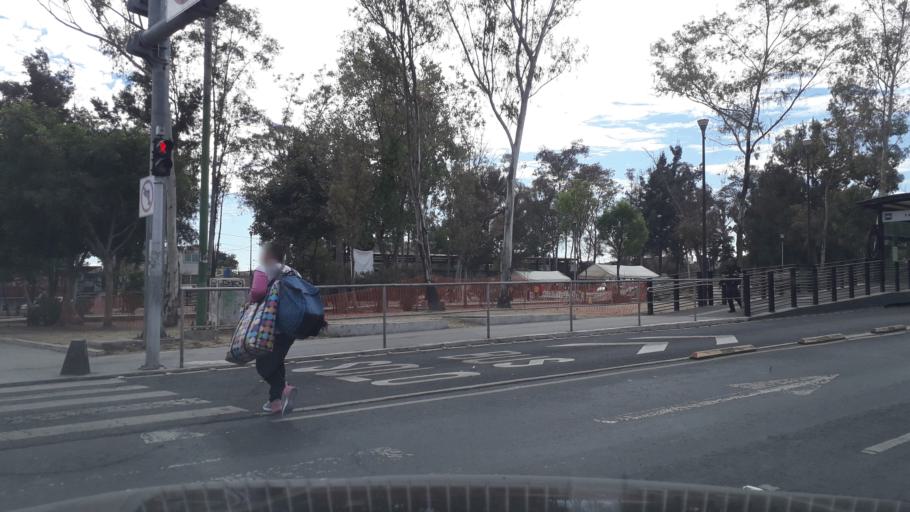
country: MX
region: Mexico City
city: Gustavo A. Madero
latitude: 19.4977
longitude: -99.0903
